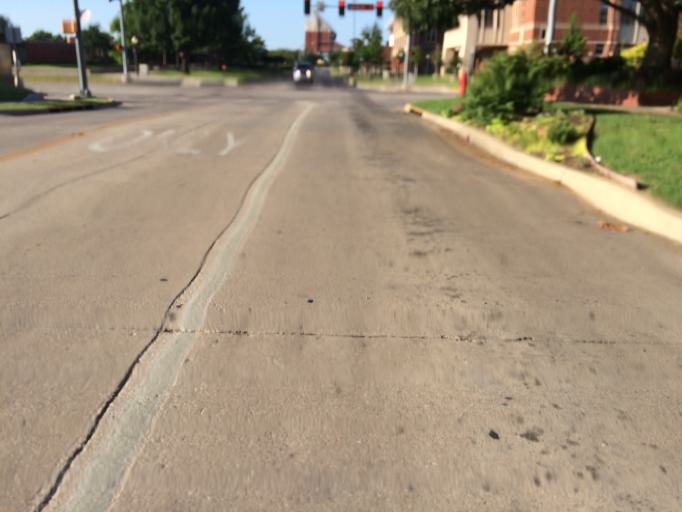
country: US
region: Oklahoma
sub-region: Cleveland County
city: Norman
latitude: 35.2116
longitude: -97.4413
